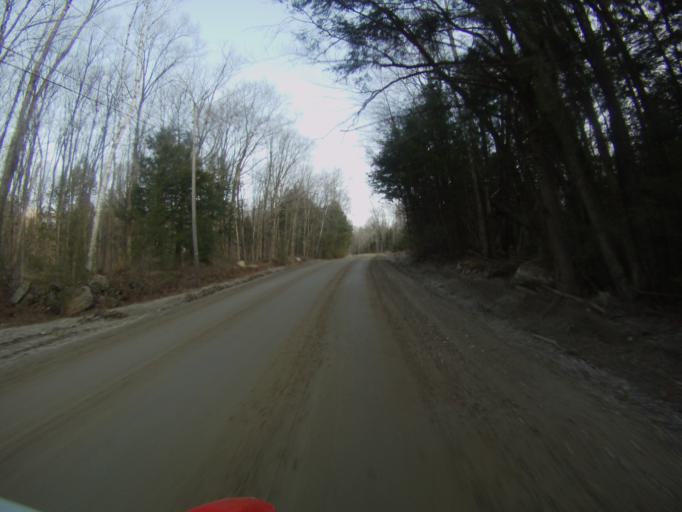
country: US
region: Vermont
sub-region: Addison County
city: Bristol
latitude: 44.0717
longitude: -73.0587
